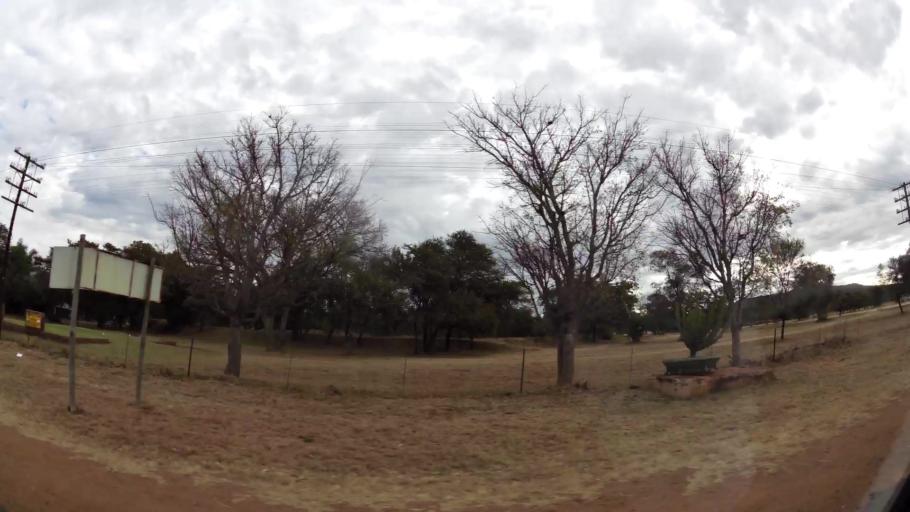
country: ZA
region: Limpopo
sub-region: Waterberg District Municipality
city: Modimolle
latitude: -24.5124
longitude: 28.7059
